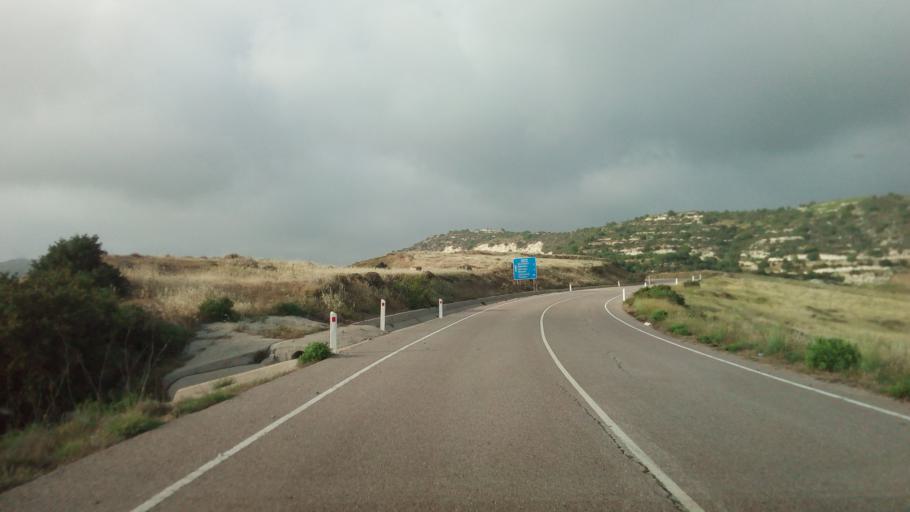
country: CY
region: Limassol
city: Pachna
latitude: 34.8222
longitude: 32.6818
